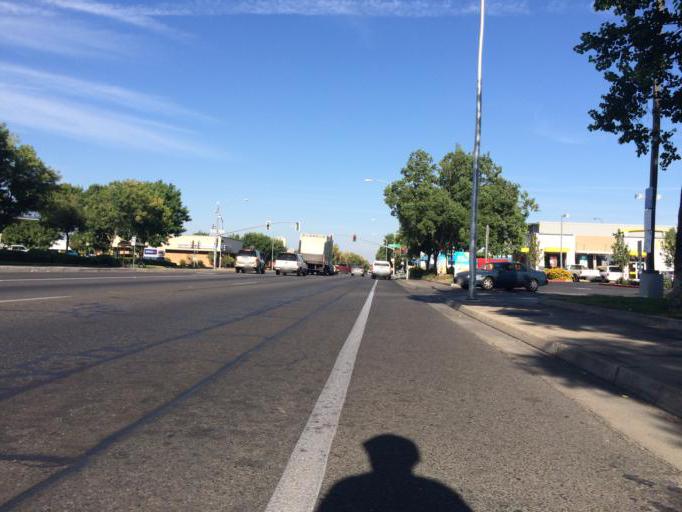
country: US
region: California
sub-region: Fresno County
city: Sunnyside
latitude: 36.7358
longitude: -119.7331
